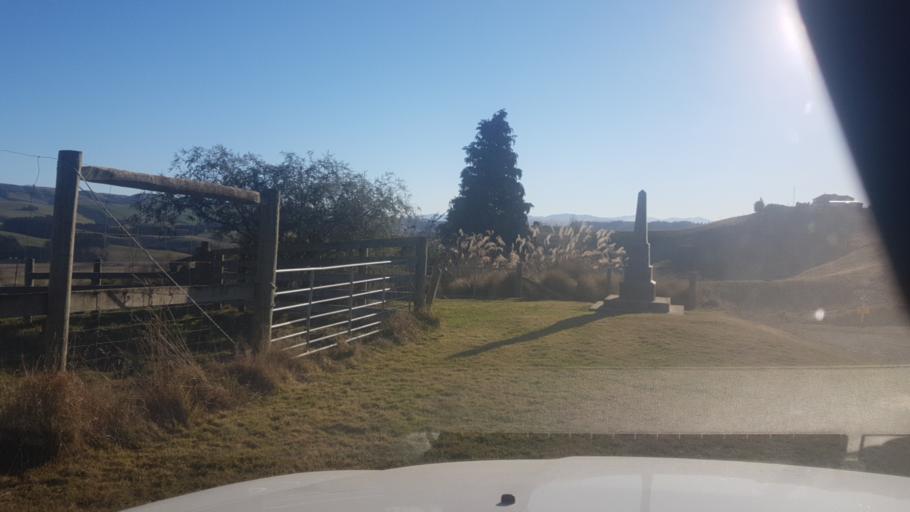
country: NZ
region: Canterbury
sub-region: Timaru District
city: Pleasant Point
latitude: -44.3430
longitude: 171.0719
